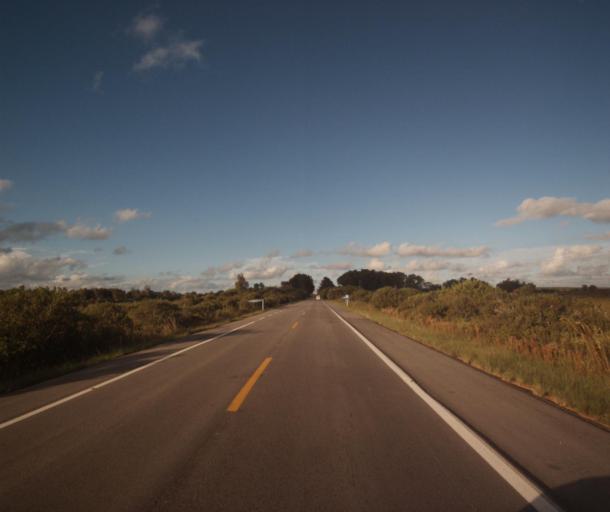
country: BR
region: Rio Grande do Sul
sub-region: Rio Grande
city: Rio Grande
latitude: -32.1271
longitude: -52.3663
